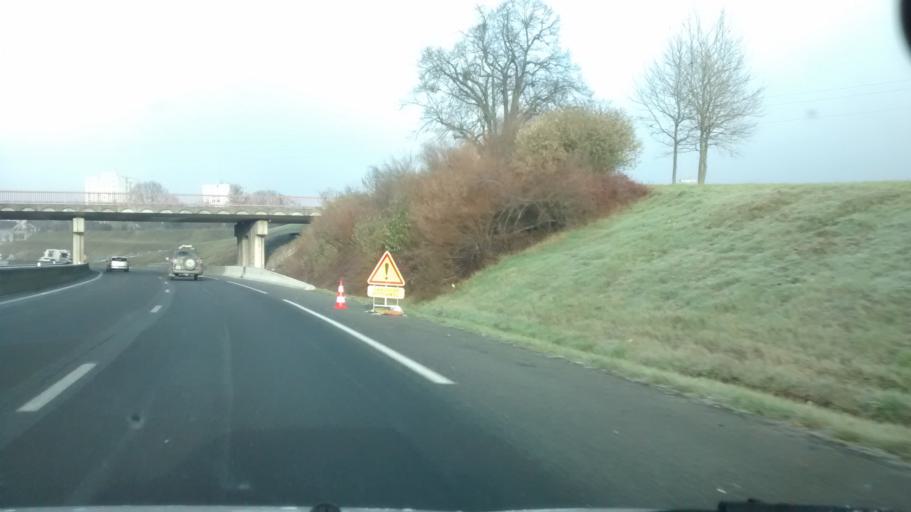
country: FR
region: Centre
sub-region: Departement d'Indre-et-Loire
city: Joue-les-Tours
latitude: 47.3391
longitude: 0.6679
